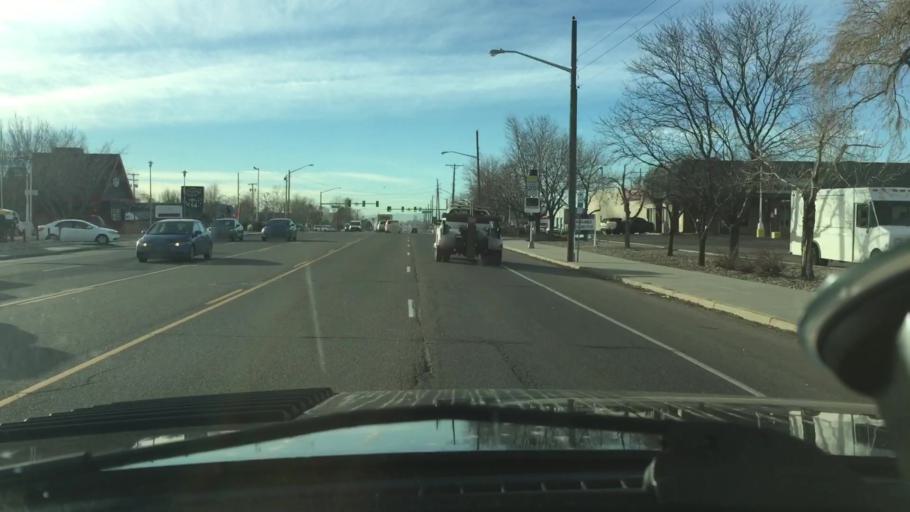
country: US
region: Colorado
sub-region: Adams County
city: Twin Lakes
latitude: 39.8256
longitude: -105.0062
